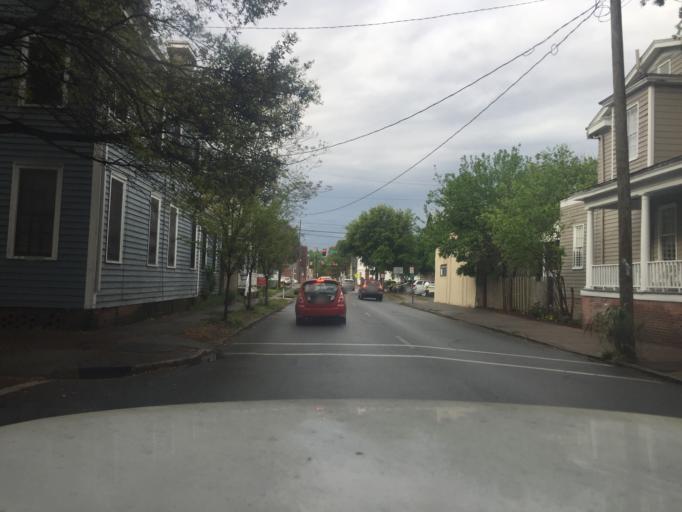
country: US
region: Georgia
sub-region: Chatham County
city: Savannah
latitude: 32.0644
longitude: -81.0986
